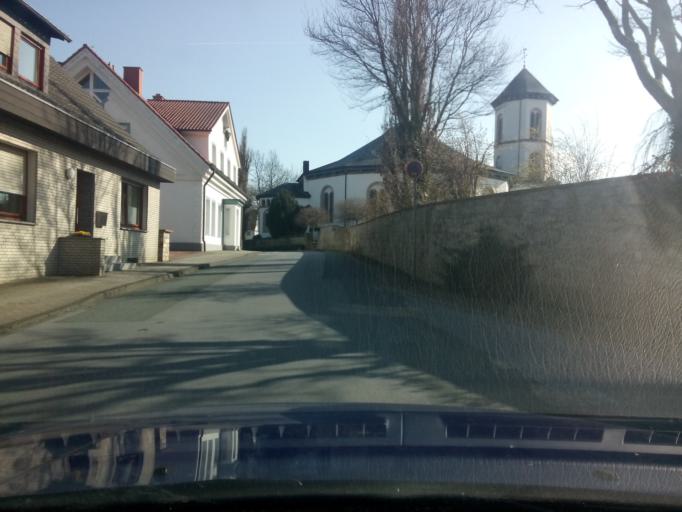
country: DE
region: Lower Saxony
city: Melle
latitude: 52.2114
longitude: 8.2728
